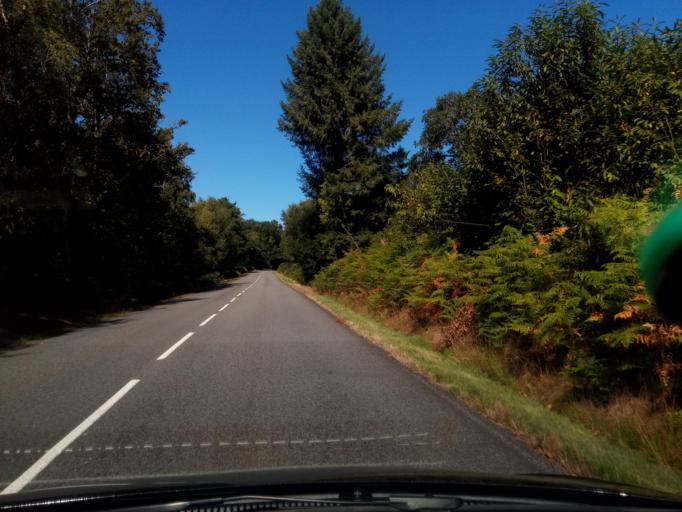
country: FR
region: Limousin
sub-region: Departement de la Haute-Vienne
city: Nantiat
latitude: 46.0664
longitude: 1.2050
